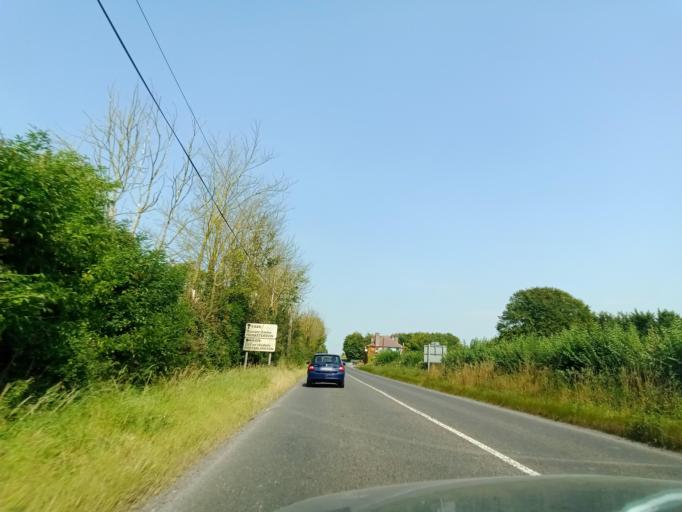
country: IE
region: Leinster
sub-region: Laois
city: Portlaoise
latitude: 53.0613
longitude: -7.2283
